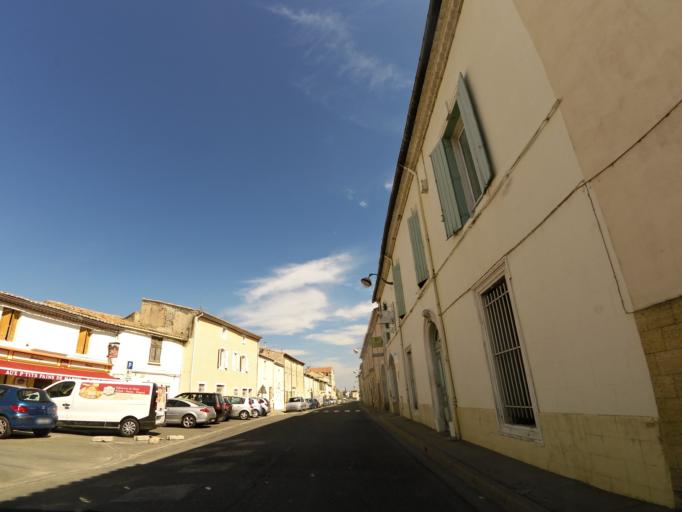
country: FR
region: Languedoc-Roussillon
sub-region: Departement du Gard
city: Uchaud
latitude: 43.7578
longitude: 4.2701
